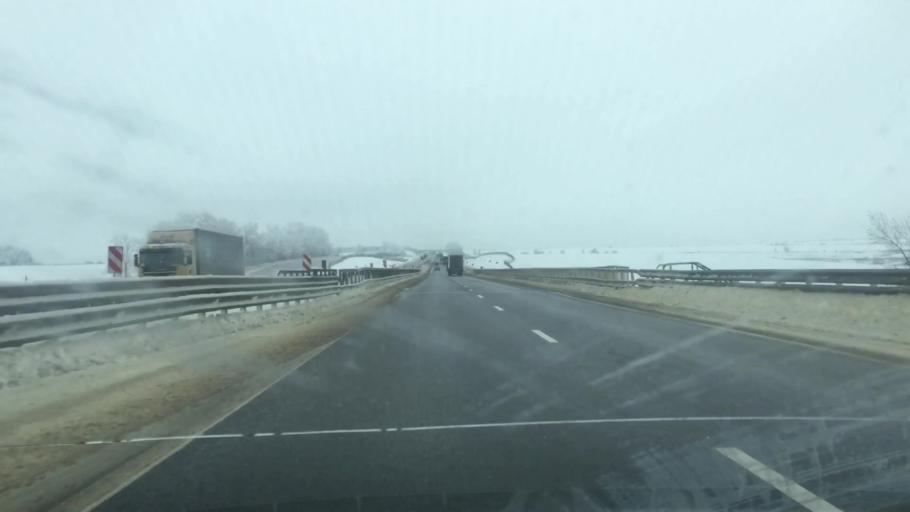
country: RU
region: Tula
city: Kazachka
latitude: 53.3304
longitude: 38.1799
